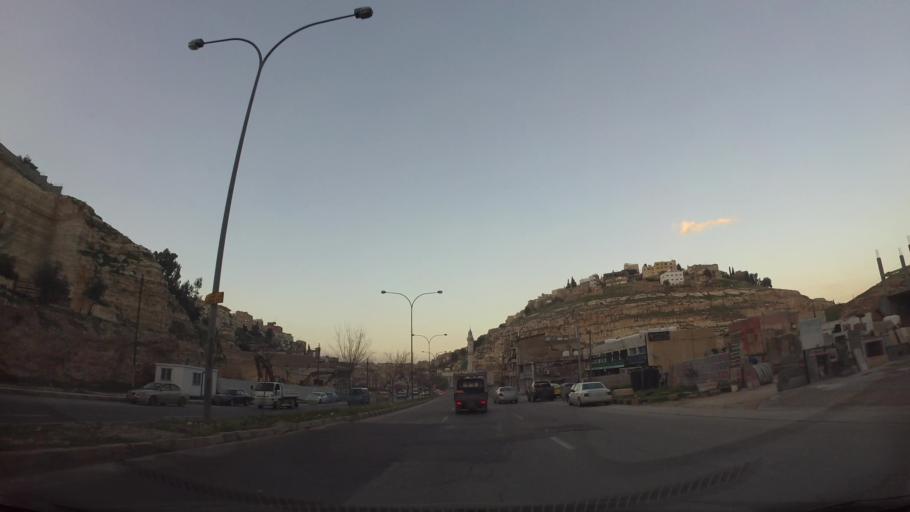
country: JO
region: Amman
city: Al Quwaysimah
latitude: 31.9300
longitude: 35.9207
